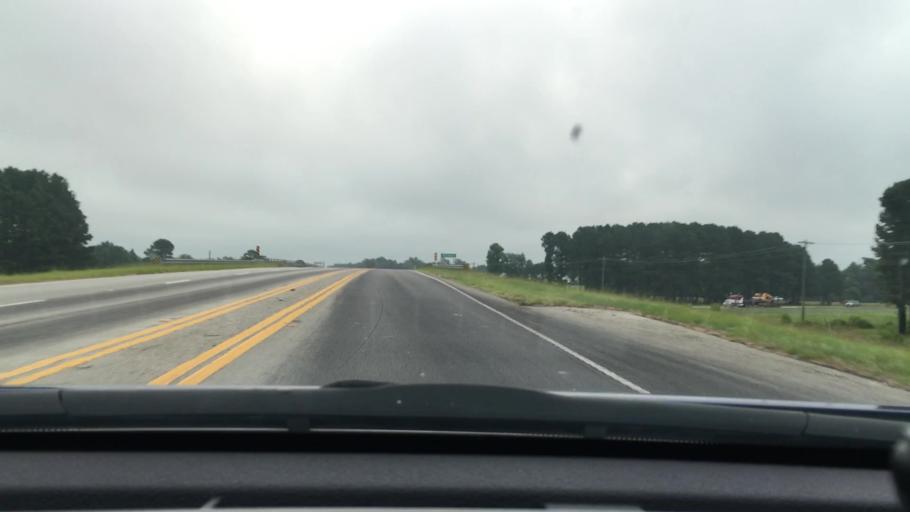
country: US
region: South Carolina
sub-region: Florence County
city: Timmonsville
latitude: 34.2053
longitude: -80.0274
